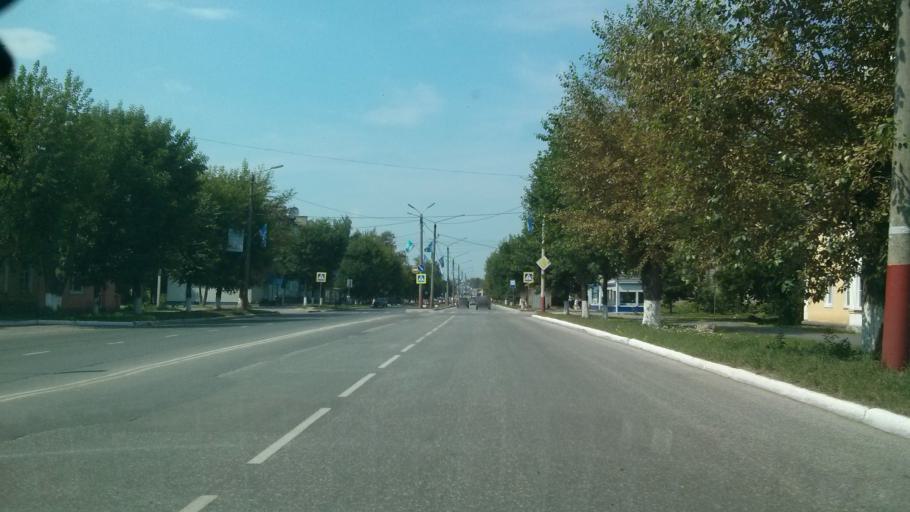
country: RU
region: Vladimir
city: Murom
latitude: 55.5687
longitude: 42.0406
